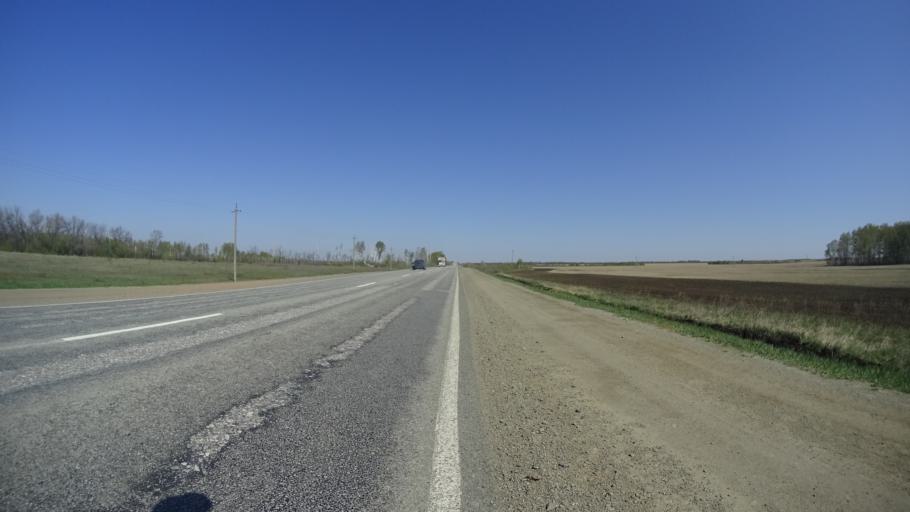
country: RU
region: Chelyabinsk
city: Troitsk
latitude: 54.1929
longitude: 61.4332
